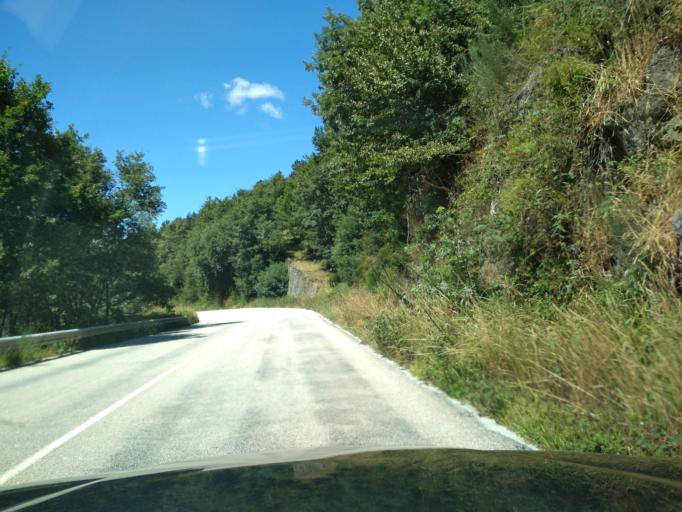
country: PT
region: Vila Real
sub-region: Ribeira de Pena
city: Ribeira de Pena
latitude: 41.5046
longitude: -7.7664
